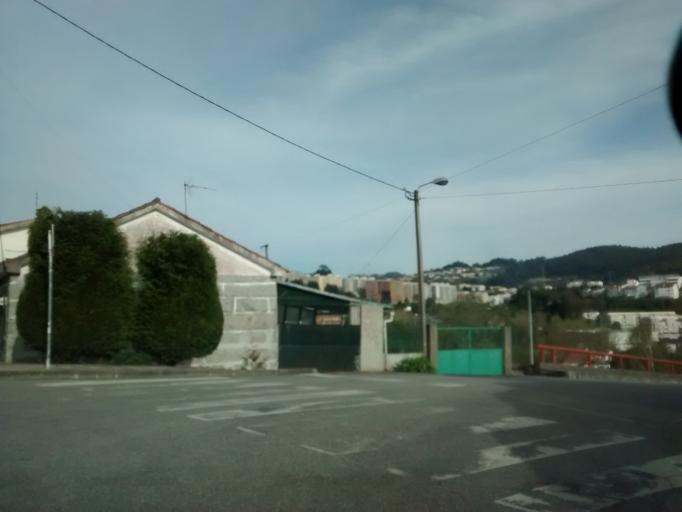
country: PT
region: Braga
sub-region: Guimaraes
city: Guimaraes
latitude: 41.4561
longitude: -8.2906
